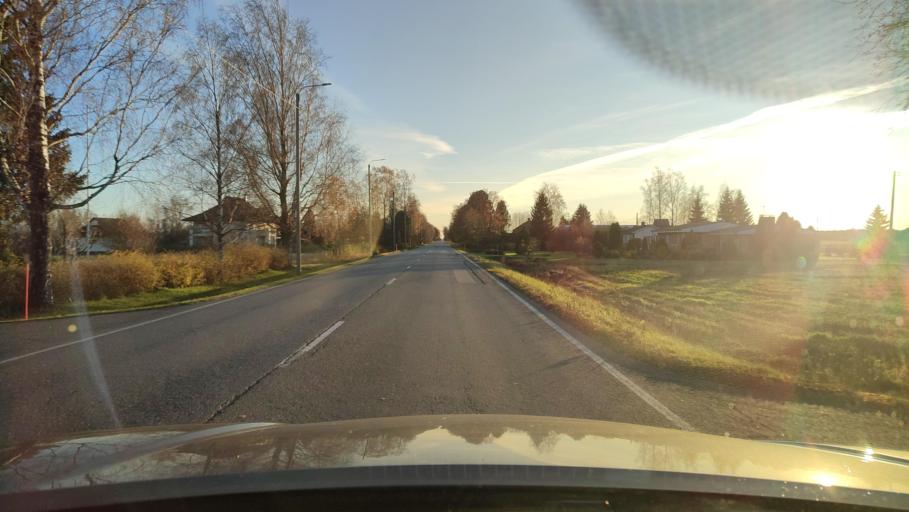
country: FI
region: Ostrobothnia
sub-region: Sydosterbotten
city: Naerpes
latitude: 62.5981
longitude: 21.4522
